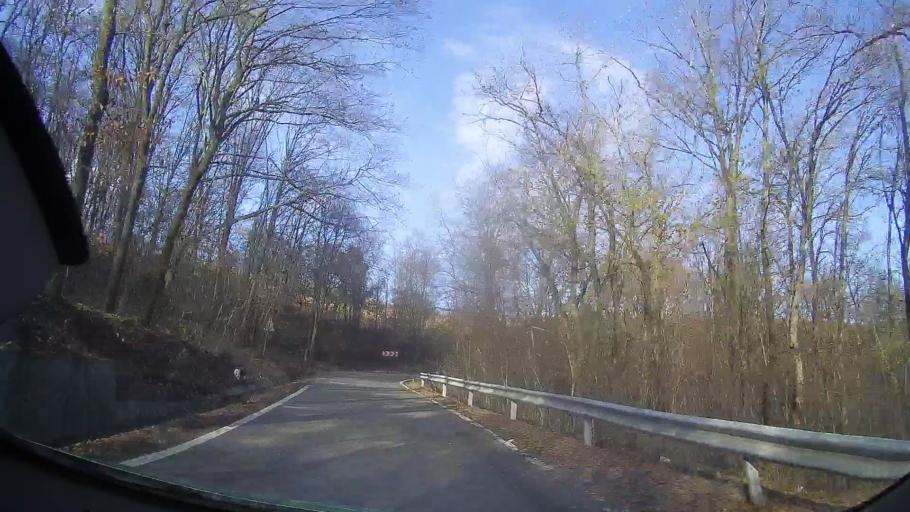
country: RO
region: Mures
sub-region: Comuna Papiu Ilarian
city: Papiu Ilarian
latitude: 46.5586
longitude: 24.1770
